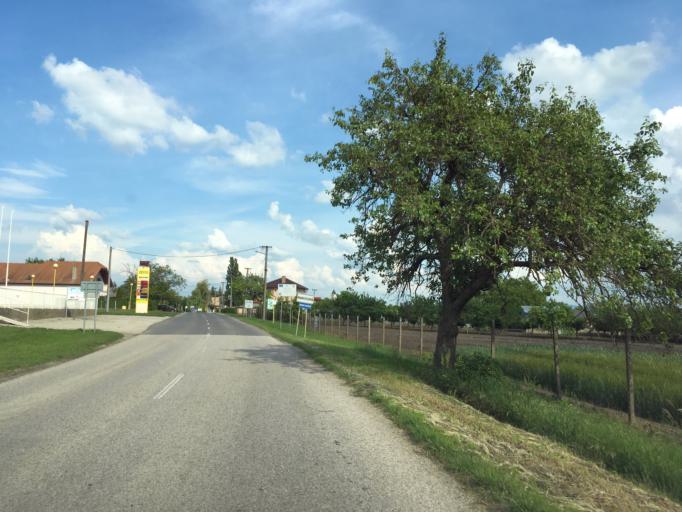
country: HU
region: Komarom-Esztergom
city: Almasfuzito
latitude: 47.7884
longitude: 18.2644
